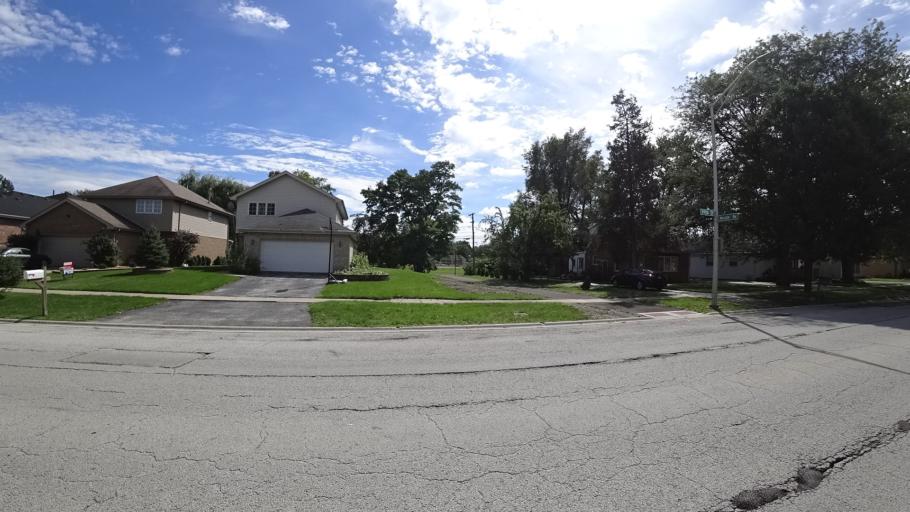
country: US
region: Illinois
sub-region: Cook County
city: Chicago Ridge
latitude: 41.7124
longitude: -87.7722
